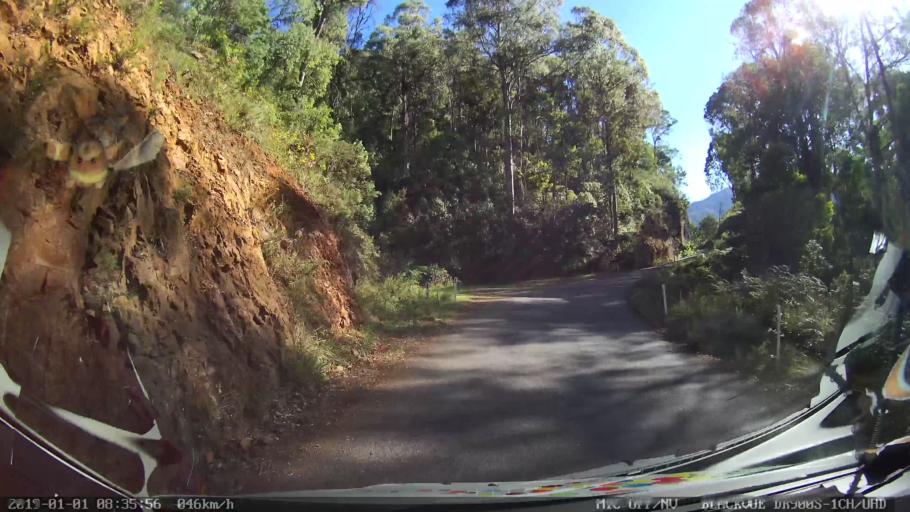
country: AU
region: New South Wales
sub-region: Snowy River
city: Jindabyne
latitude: -36.3464
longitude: 148.1936
